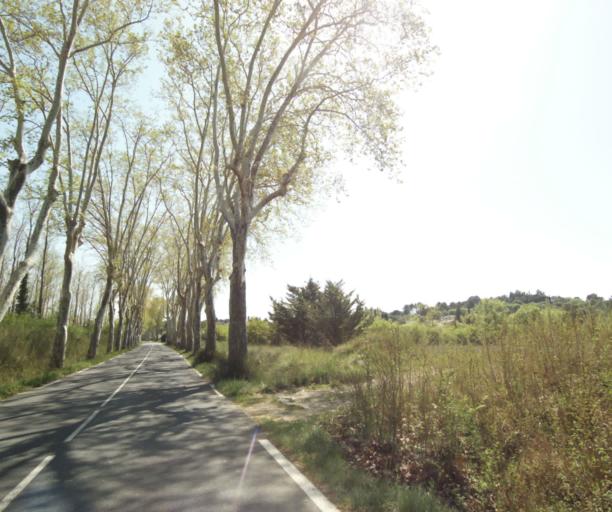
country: FR
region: Languedoc-Roussillon
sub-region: Departement de l'Herault
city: Montferrier-sur-Lez
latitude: 43.6590
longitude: 3.8633
